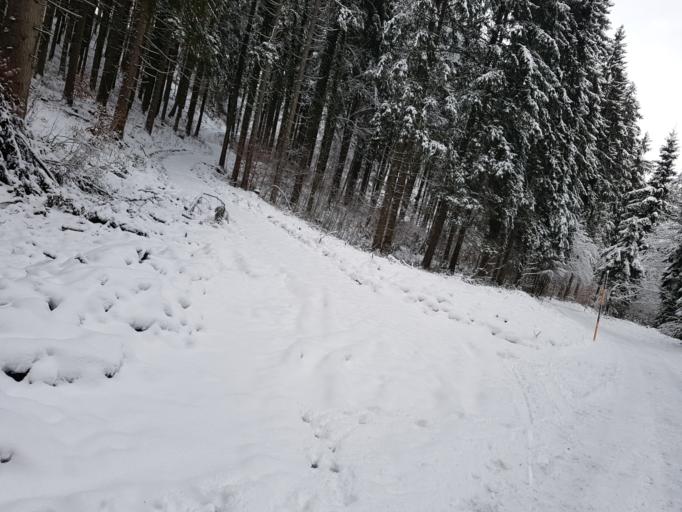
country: DE
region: Bavaria
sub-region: Upper Bavaria
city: Bayerisch Gmain
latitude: 47.7266
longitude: 12.9384
